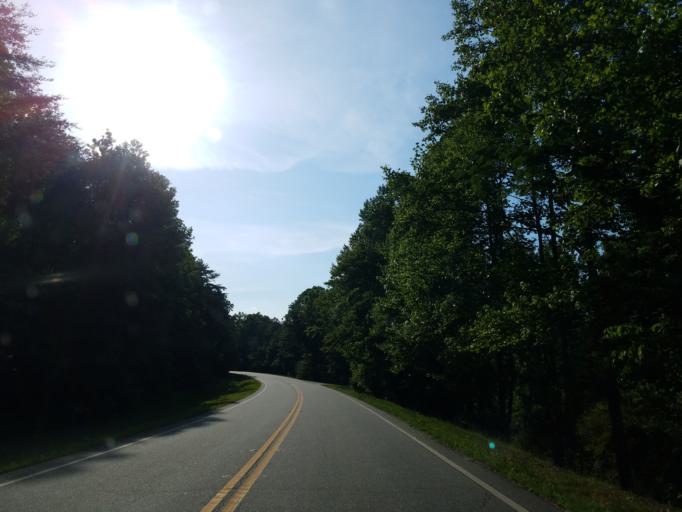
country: US
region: Georgia
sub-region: Whitfield County
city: Dalton
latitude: 34.6757
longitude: -85.0651
